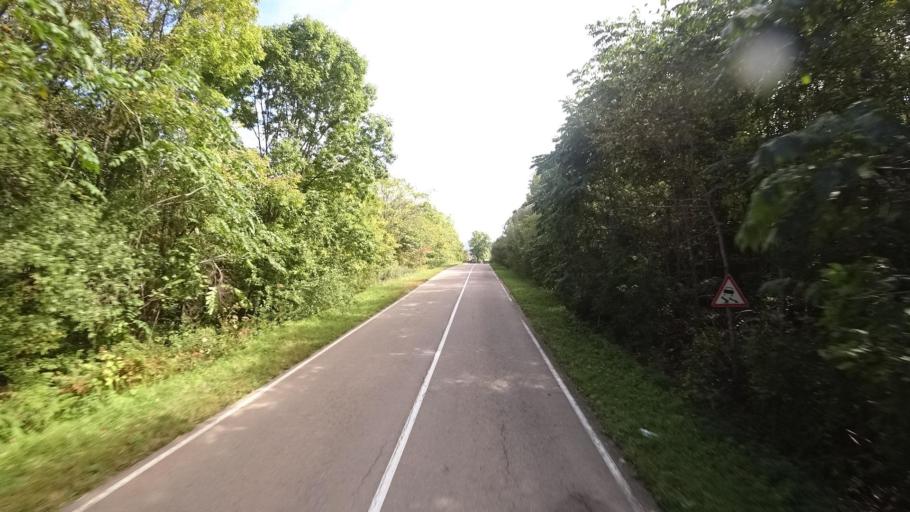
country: RU
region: Primorskiy
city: Yakovlevka
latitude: 44.4007
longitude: 133.5970
